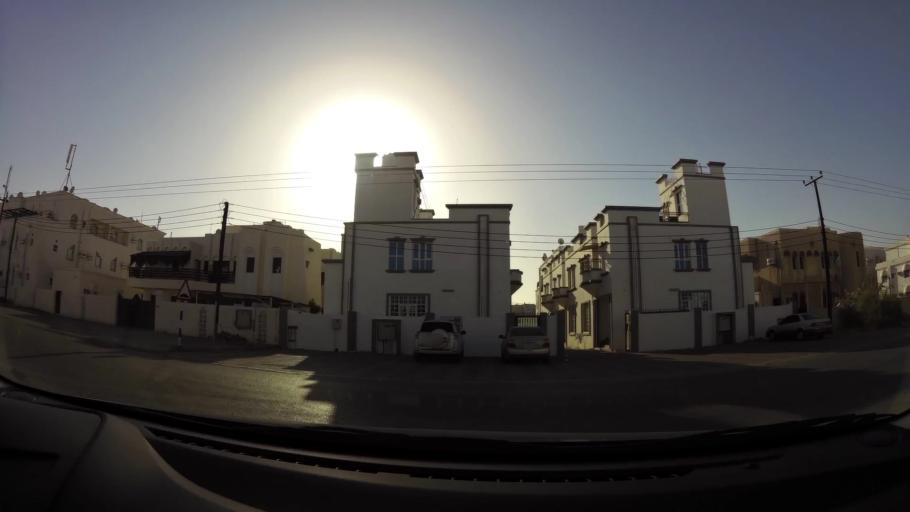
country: OM
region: Muhafazat Masqat
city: As Sib al Jadidah
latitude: 23.6368
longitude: 58.1975
